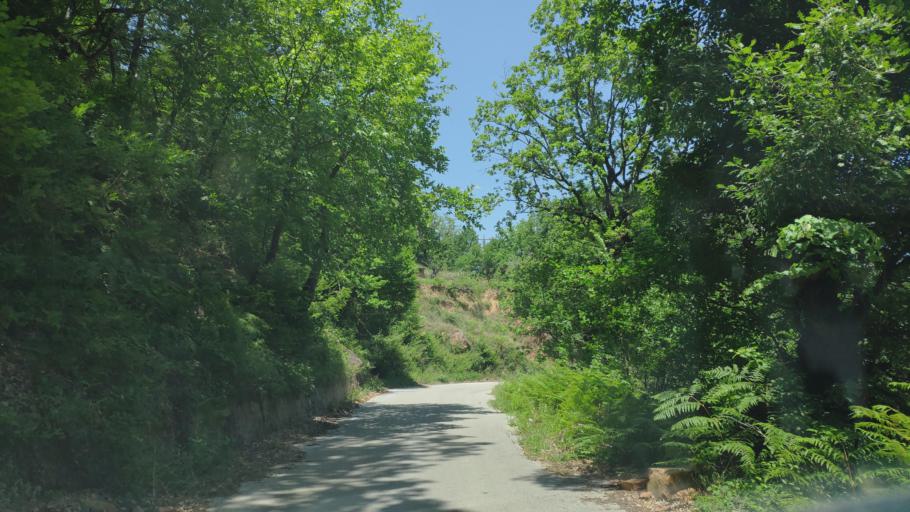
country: GR
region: Epirus
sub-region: Nomos Artas
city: Ano Kalentini
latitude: 39.1977
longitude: 21.3434
